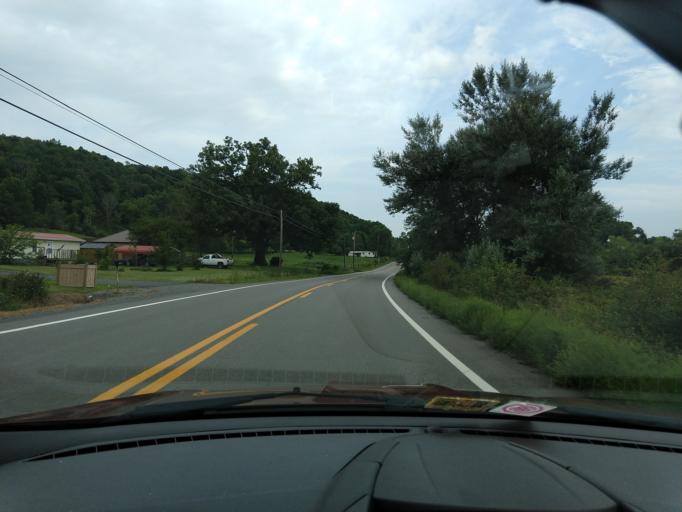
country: US
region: West Virginia
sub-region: Greenbrier County
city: Rainelle
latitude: 37.9434
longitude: -80.6518
